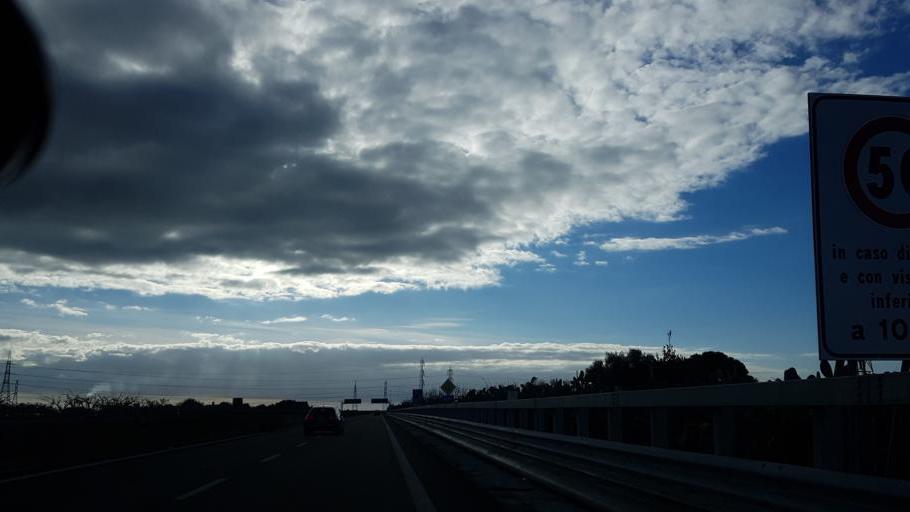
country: IT
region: Apulia
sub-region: Provincia di Brindisi
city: La Rosa
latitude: 40.6122
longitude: 17.9599
